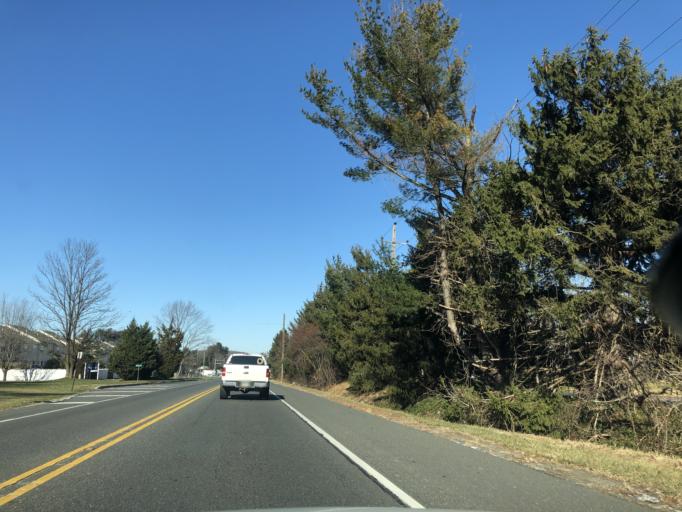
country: US
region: Pennsylvania
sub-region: Bucks County
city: Hulmeville
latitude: 40.1535
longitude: -74.8932
